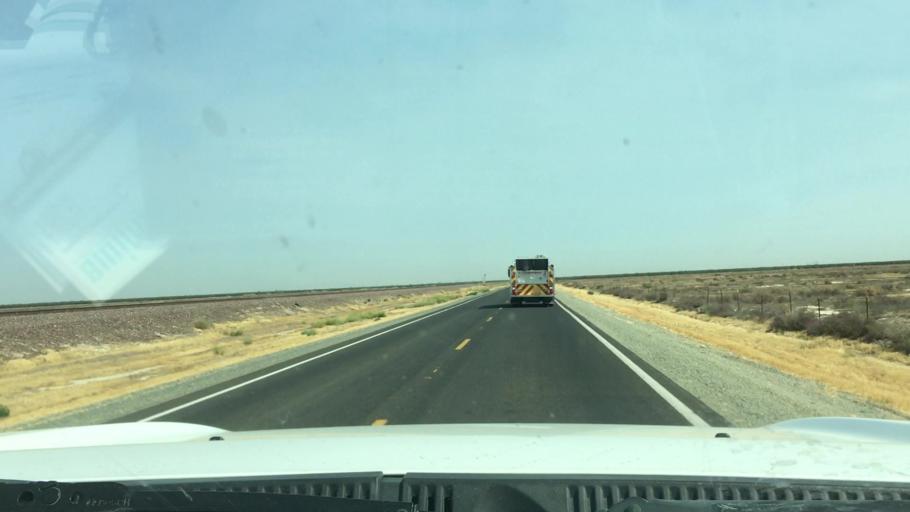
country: US
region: California
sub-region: Kern County
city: Delano
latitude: 35.7987
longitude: -119.3581
